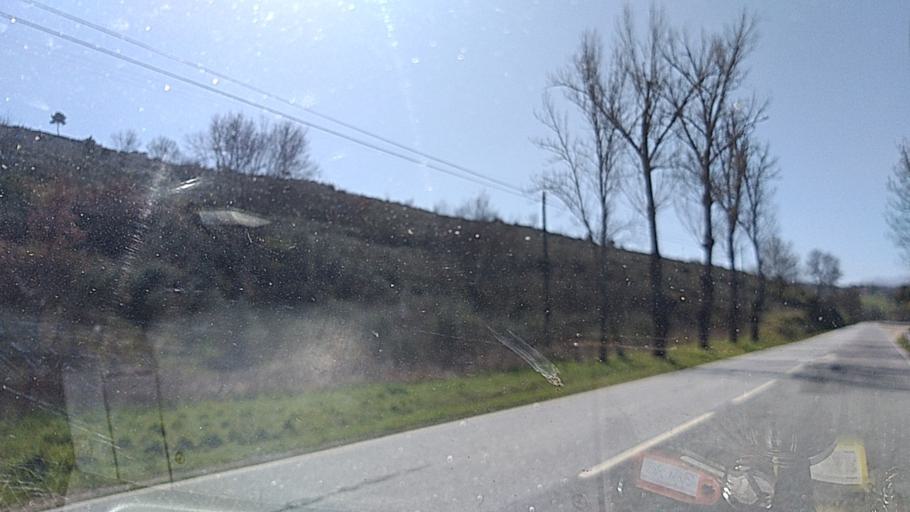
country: PT
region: Guarda
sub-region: Celorico da Beira
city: Celorico da Beira
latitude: 40.6035
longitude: -7.4230
